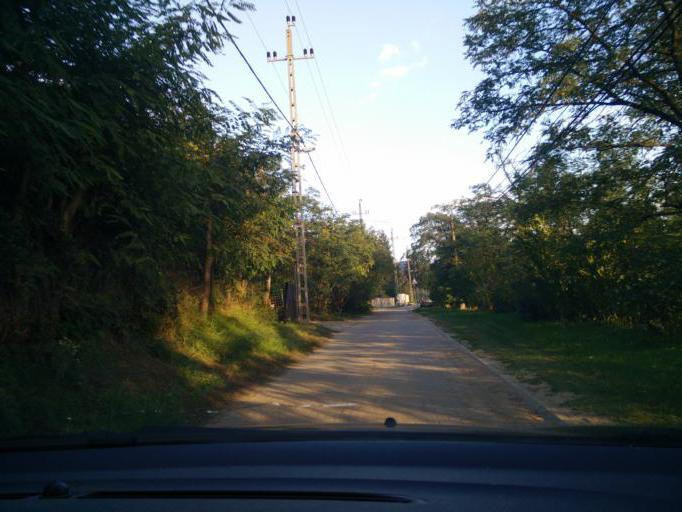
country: HU
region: Pest
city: Piliscsaba
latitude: 47.6338
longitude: 18.8357
